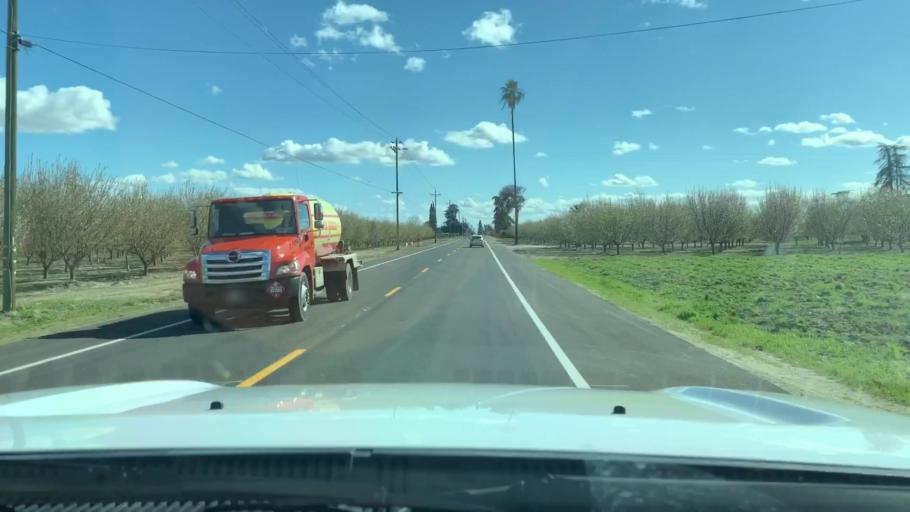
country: US
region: California
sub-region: Fresno County
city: Fowler
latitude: 36.5894
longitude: -119.6825
